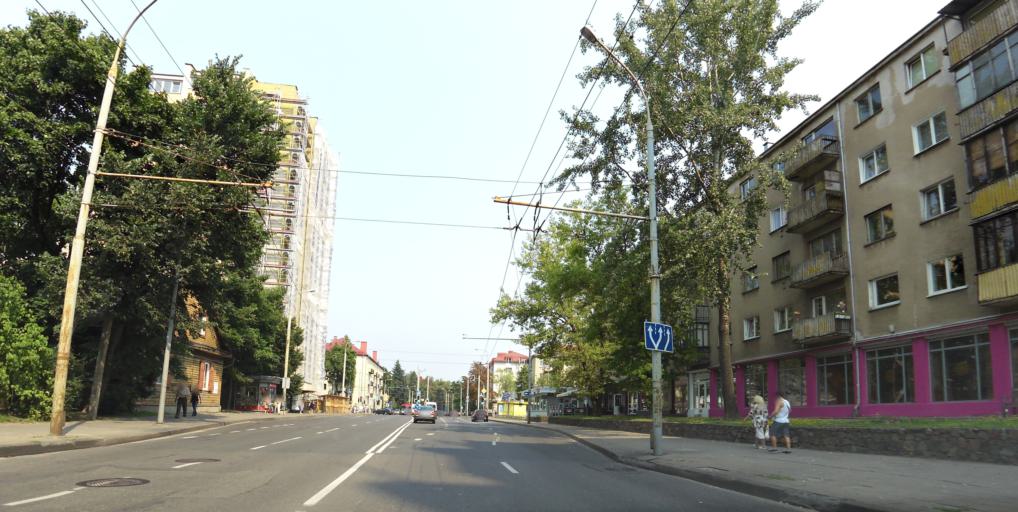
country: LT
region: Vilnius County
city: Rasos
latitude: 54.7040
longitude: 25.3102
